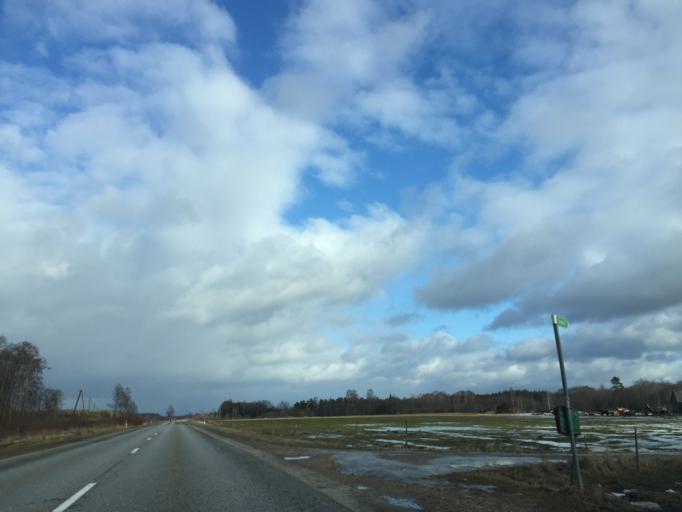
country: LV
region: Aloja
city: Staicele
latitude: 57.8727
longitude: 24.5758
